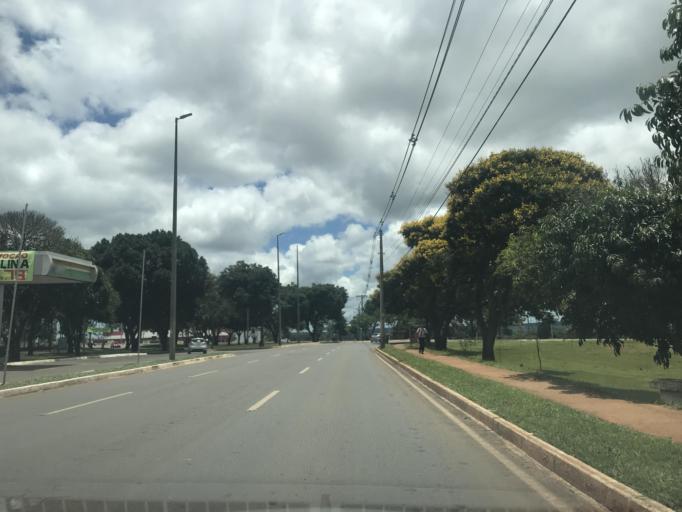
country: BR
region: Federal District
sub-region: Brasilia
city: Brasilia
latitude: -15.6524
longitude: -47.7839
